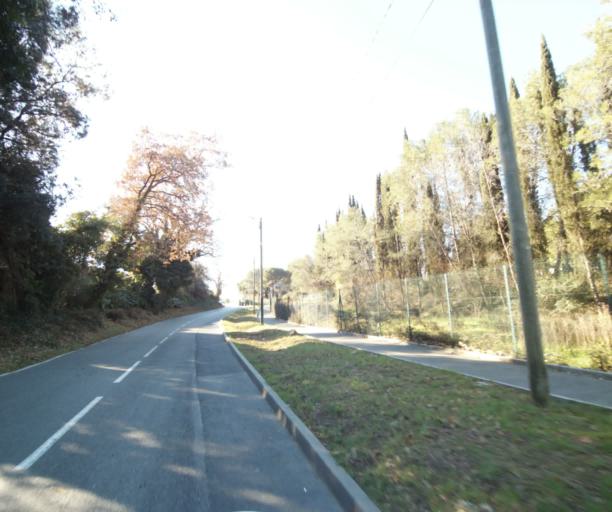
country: FR
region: Provence-Alpes-Cote d'Azur
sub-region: Departement des Alpes-Maritimes
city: Vallauris
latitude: 43.5996
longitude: 7.0759
